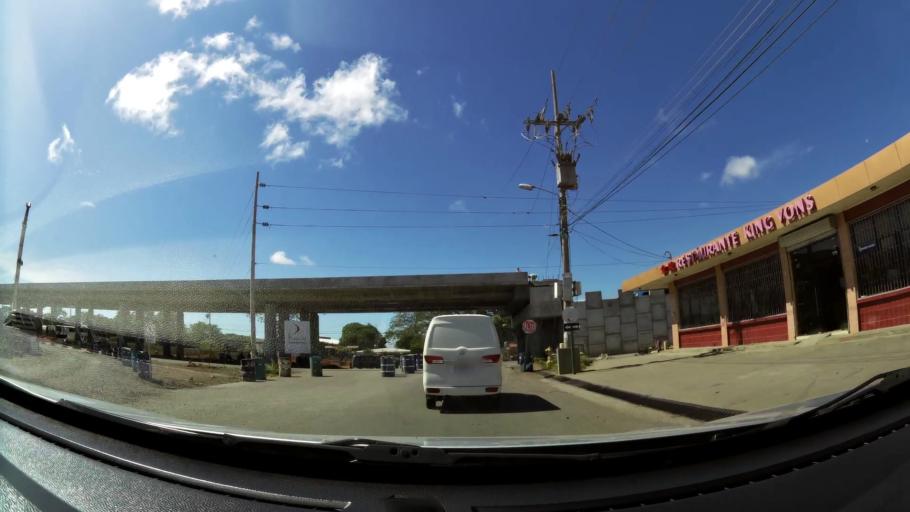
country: CR
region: Guanacaste
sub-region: Canton de Canas
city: Canas
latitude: 10.4284
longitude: -85.0945
